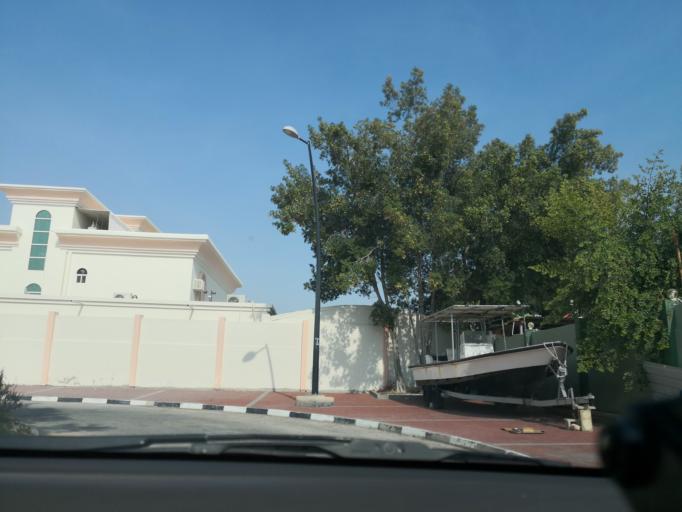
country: QA
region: Baladiyat ad Dawhah
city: Doha
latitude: 25.3471
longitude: 51.4965
